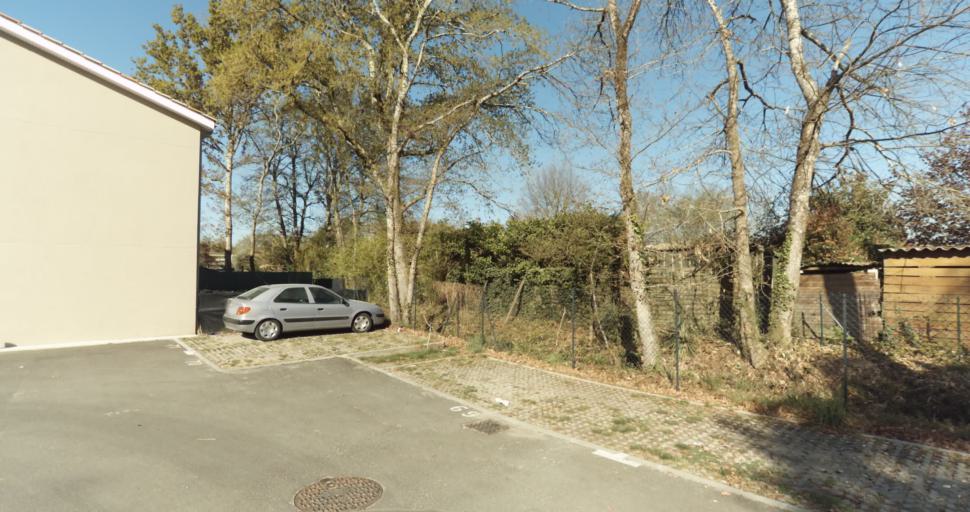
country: FR
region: Aquitaine
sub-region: Departement de la Gironde
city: Martignas-sur-Jalle
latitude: 44.7995
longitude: -0.8364
